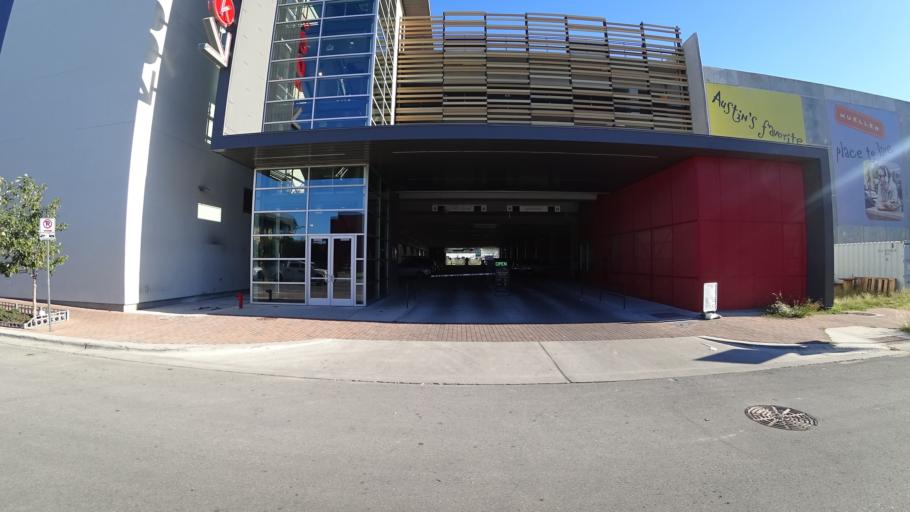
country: US
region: Texas
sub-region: Travis County
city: Austin
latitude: 30.2981
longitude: -97.7045
